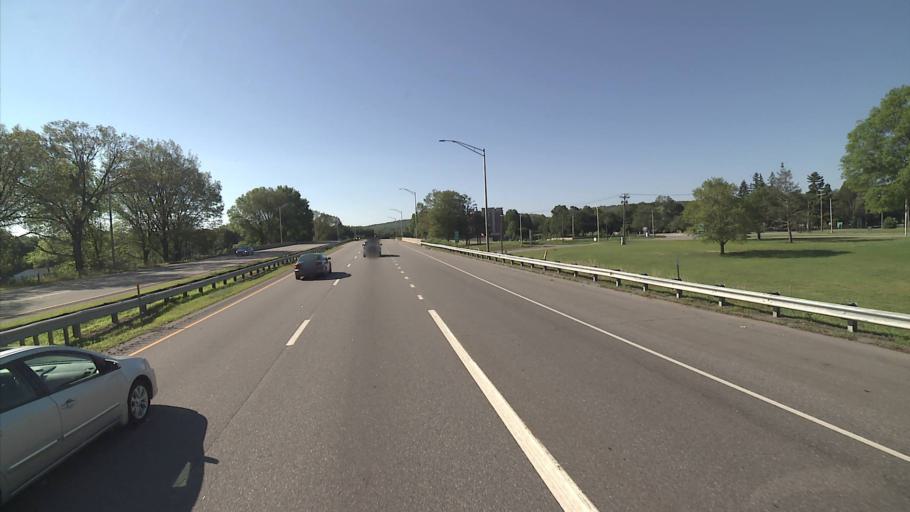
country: US
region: Connecticut
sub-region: New London County
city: Norwich
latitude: 41.5108
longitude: -72.1171
